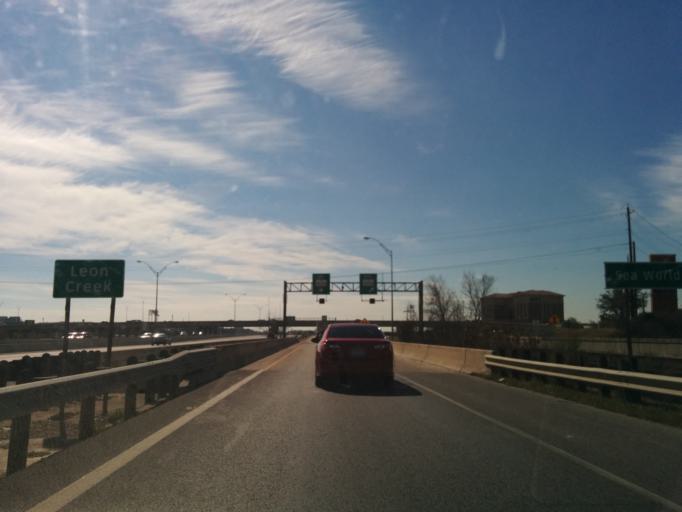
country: US
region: Texas
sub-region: Bexar County
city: Shavano Park
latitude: 29.5939
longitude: -98.5991
